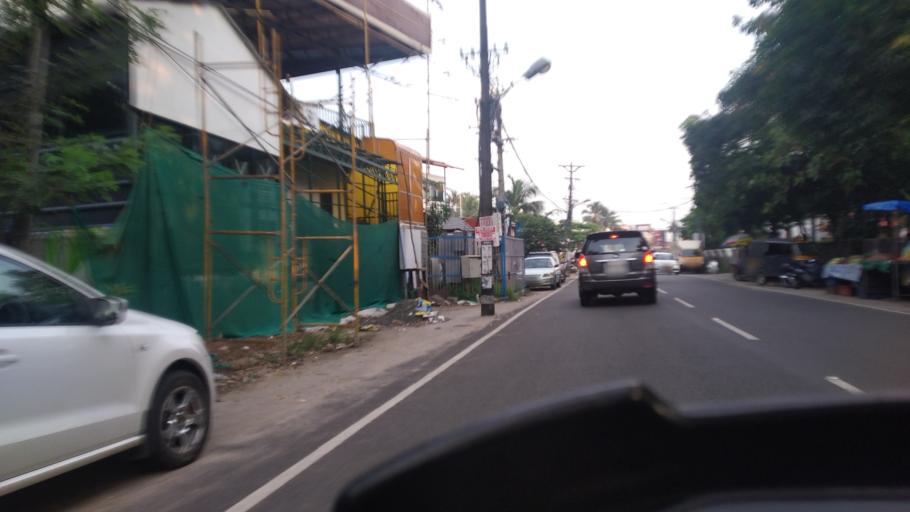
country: IN
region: Kerala
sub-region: Ernakulam
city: Elur
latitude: 10.0297
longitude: 76.3047
